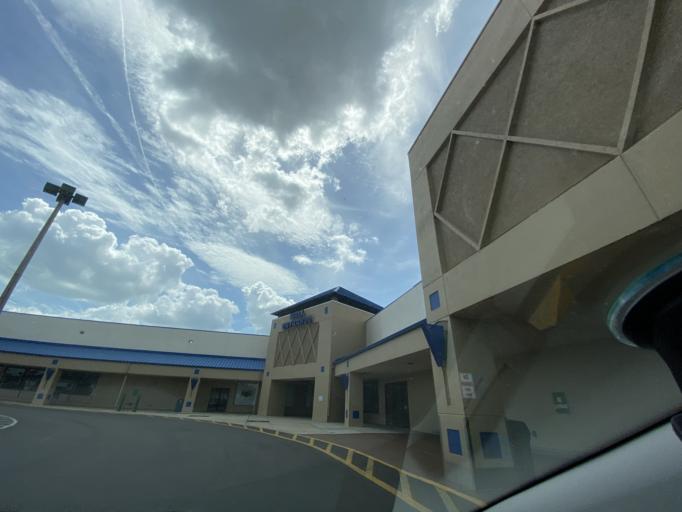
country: US
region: Florida
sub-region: Volusia County
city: South Daytona
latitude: 29.1652
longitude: -81.0012
